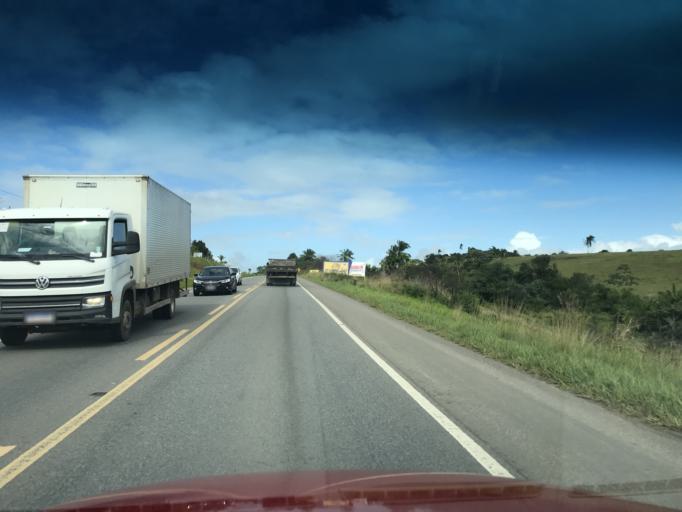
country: BR
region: Bahia
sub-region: Conceicao Do Almeida
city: Muritiba
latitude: -12.9170
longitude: -39.2450
